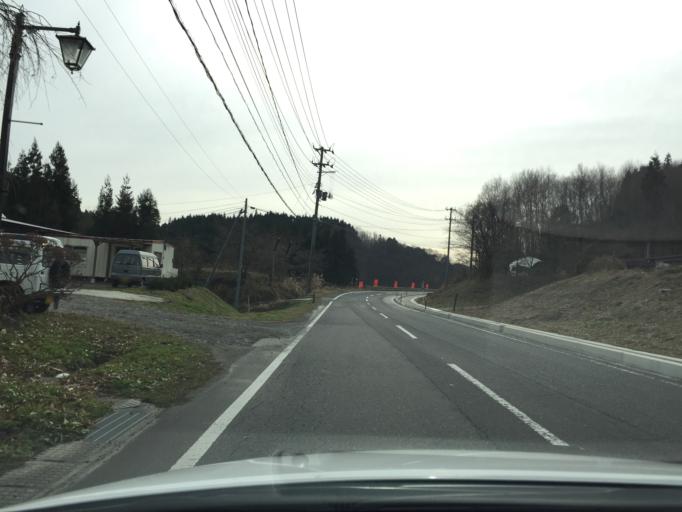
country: JP
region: Fukushima
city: Ishikawa
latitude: 37.2255
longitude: 140.5680
